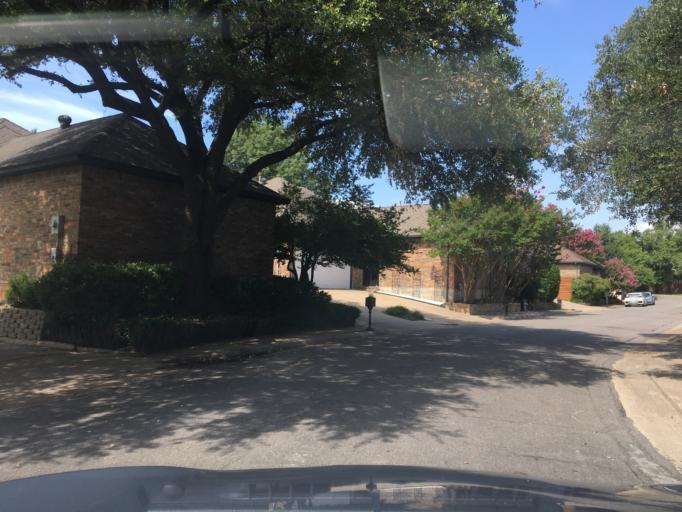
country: US
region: Texas
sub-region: Dallas County
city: Addison
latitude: 32.9265
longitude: -96.7980
